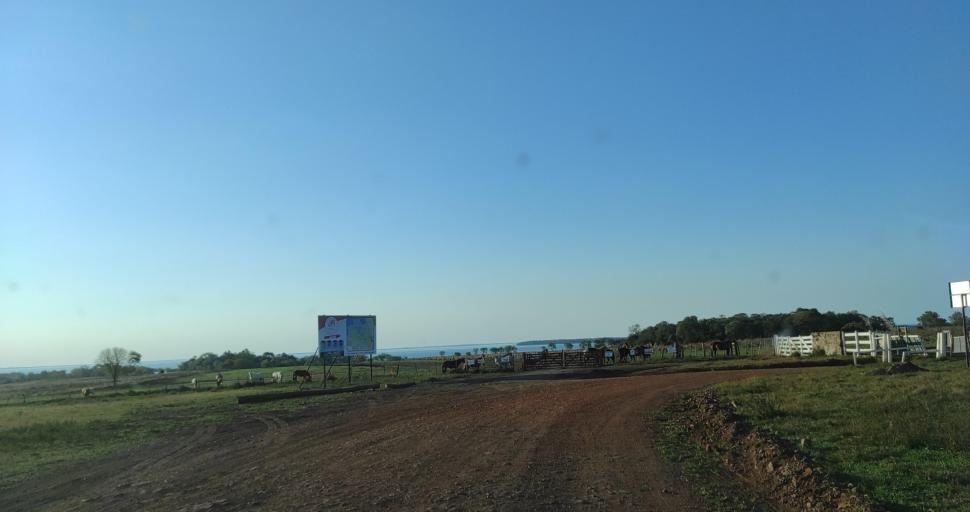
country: PY
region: Itapua
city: Carmen del Parana
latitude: -27.4082
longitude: -56.1653
